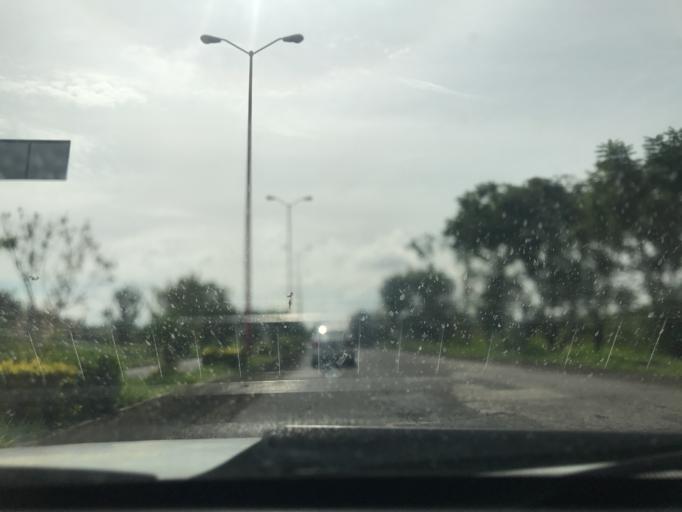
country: MX
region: Morelos
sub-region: Atlatlahucan
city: Colonia San Francisco
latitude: 18.8968
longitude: -98.9071
